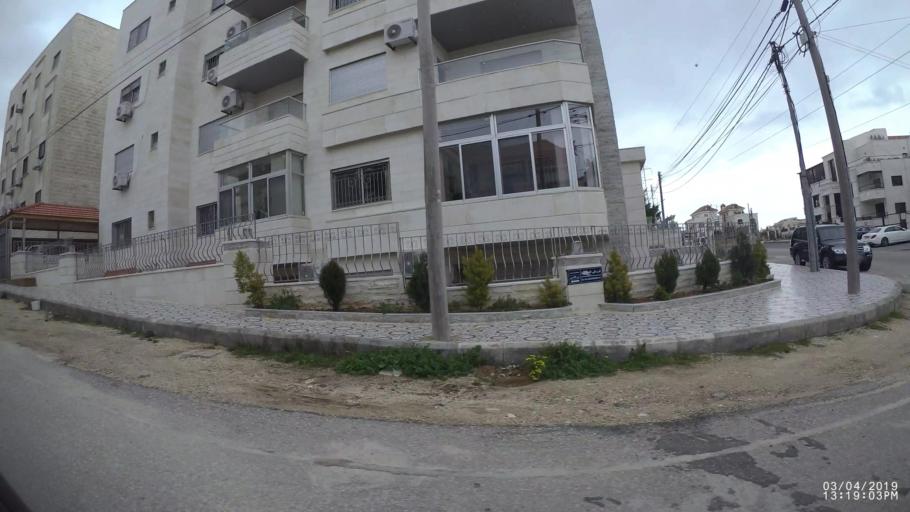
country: JO
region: Amman
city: Wadi as Sir
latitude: 31.9650
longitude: 35.8247
